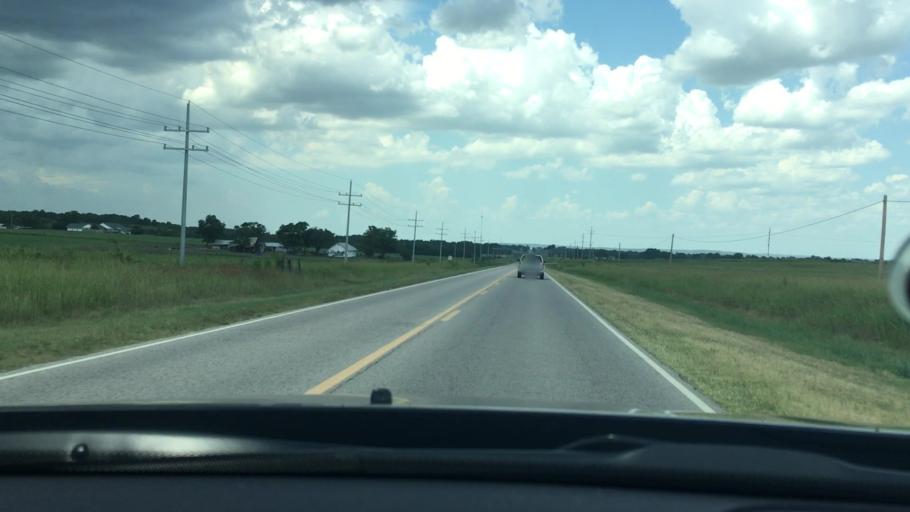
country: US
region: Oklahoma
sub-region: Pontotoc County
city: Ada
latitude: 34.6327
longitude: -96.6349
